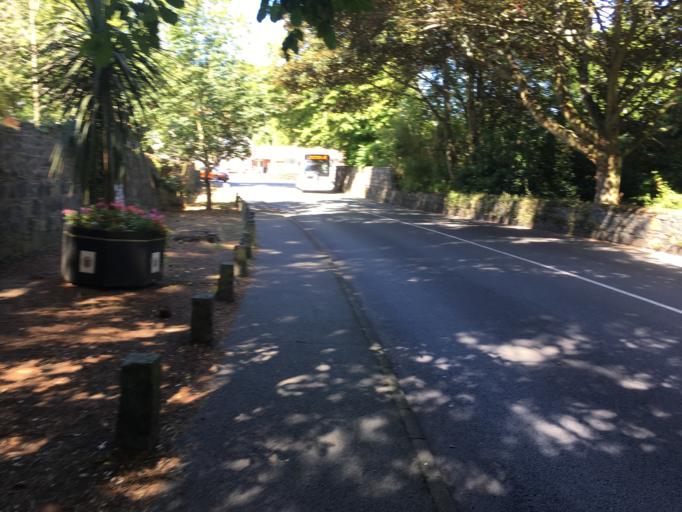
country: GG
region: St Peter Port
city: Saint Peter Port
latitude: 49.4604
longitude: -2.5621
